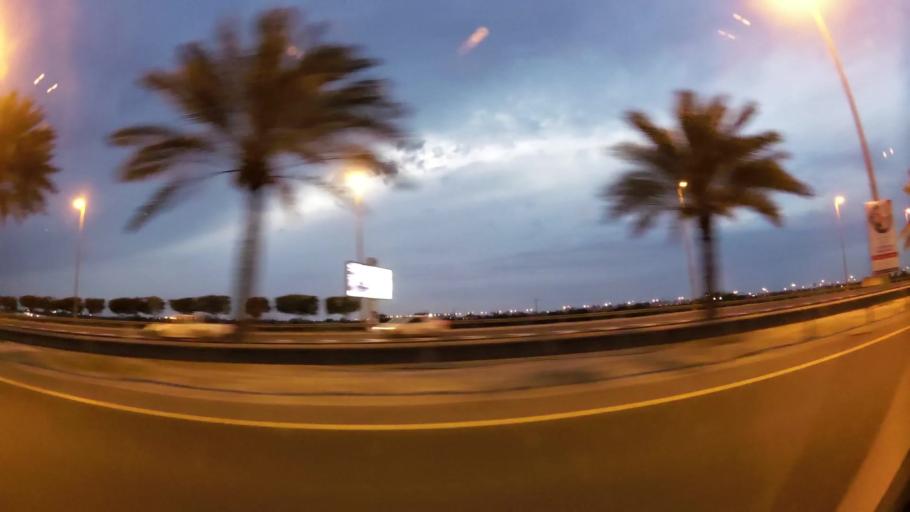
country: BH
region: Northern
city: Madinat `Isa
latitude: 26.1763
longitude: 50.5024
